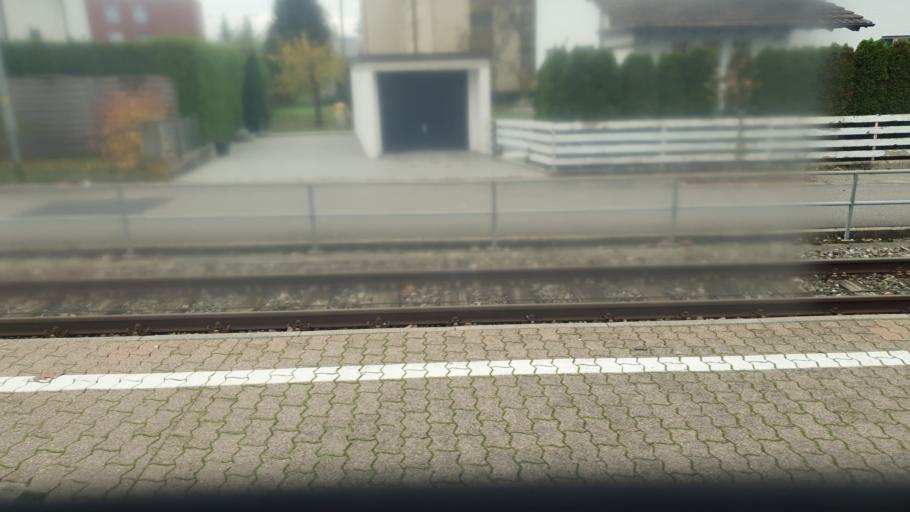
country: CH
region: Aargau
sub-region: Bezirk Aarau
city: Oberentfelden
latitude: 47.3609
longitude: 8.0459
